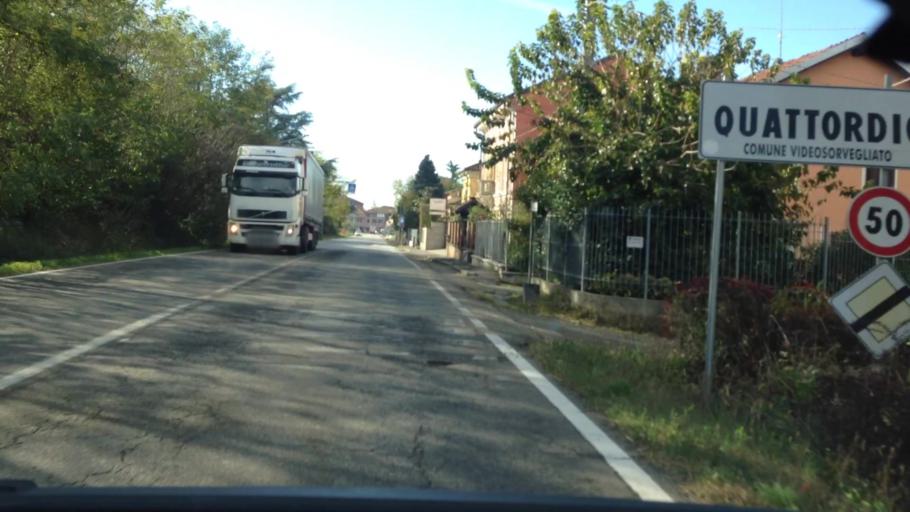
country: IT
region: Piedmont
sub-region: Provincia di Alessandria
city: Quattordio
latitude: 44.8991
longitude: 8.4154
